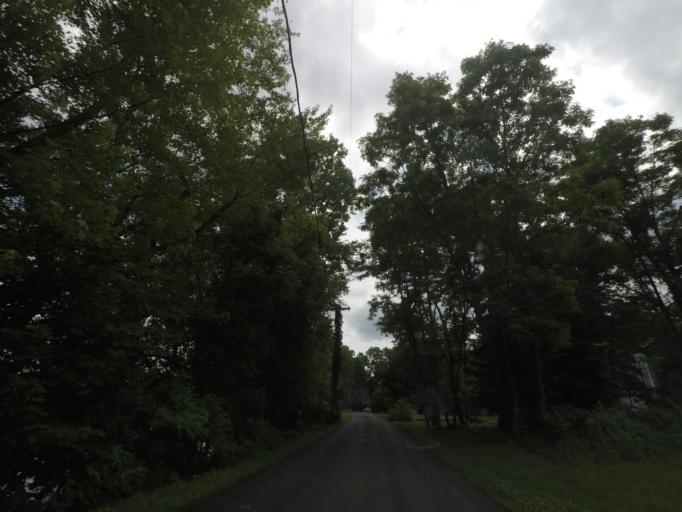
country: US
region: New York
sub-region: Saratoga County
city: Stillwater
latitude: 42.9881
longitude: -73.6096
